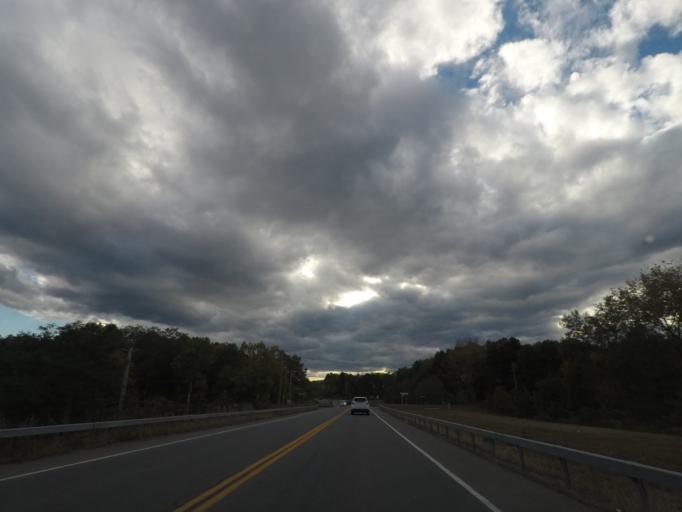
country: US
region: New York
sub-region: Albany County
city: Colonie
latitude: 42.7245
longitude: -73.8618
